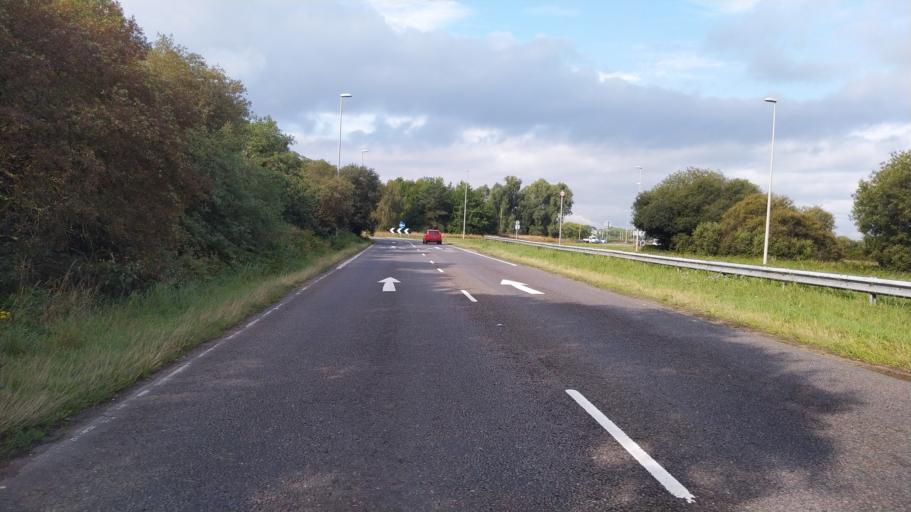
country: GB
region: England
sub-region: Dorset
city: Christchurch
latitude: 50.7404
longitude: -1.7669
